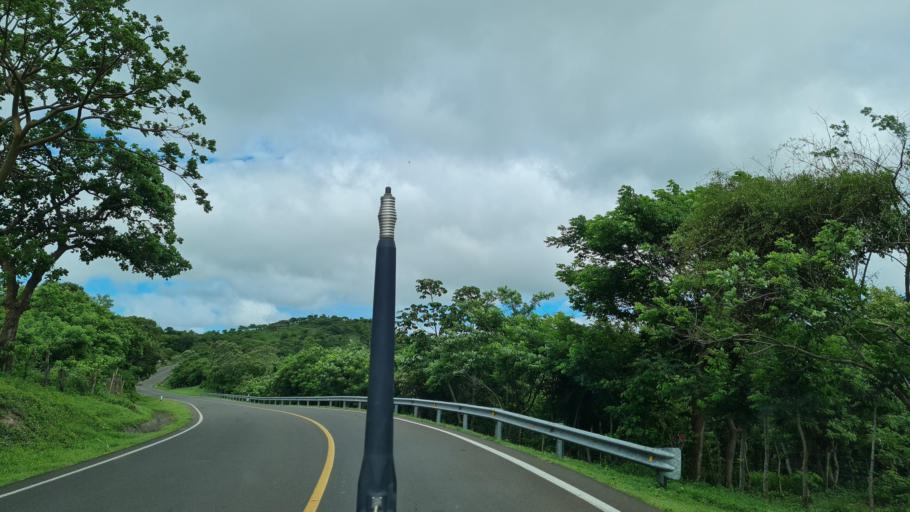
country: NI
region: Matagalpa
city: Terrabona
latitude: 12.5930
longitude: -85.9504
